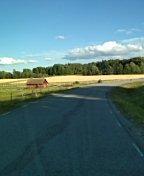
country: SE
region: Uppsala
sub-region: Enkopings Kommun
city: Grillby
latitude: 59.6813
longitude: 17.2173
